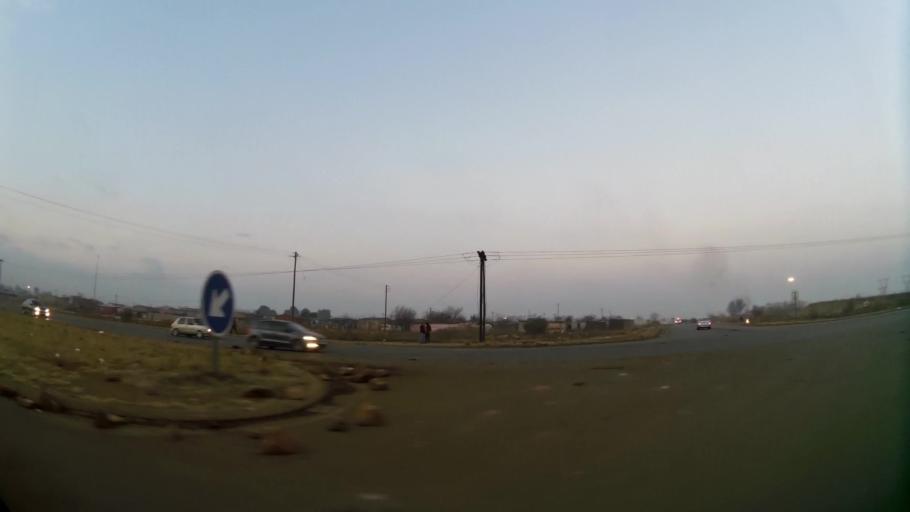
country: ZA
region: Gauteng
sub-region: City of Johannesburg Metropolitan Municipality
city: Orange Farm
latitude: -26.5500
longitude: 27.8303
